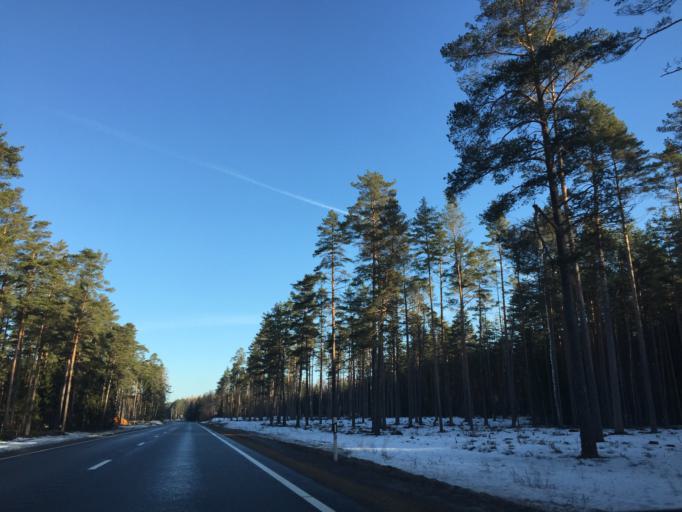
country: LV
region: Salacgrivas
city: Salacgriva
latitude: 57.5640
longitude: 24.4342
